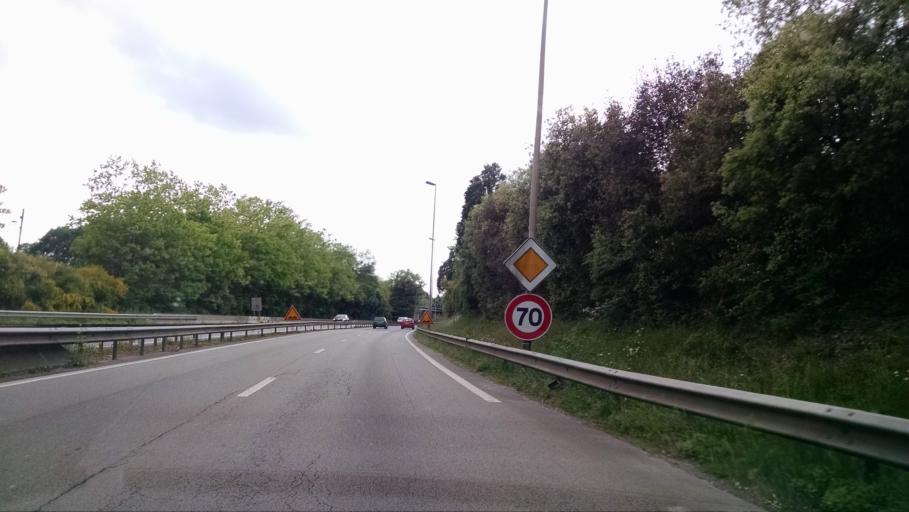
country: FR
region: Pays de la Loire
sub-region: Departement de la Loire-Atlantique
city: Nantes
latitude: 47.2553
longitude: -1.5350
